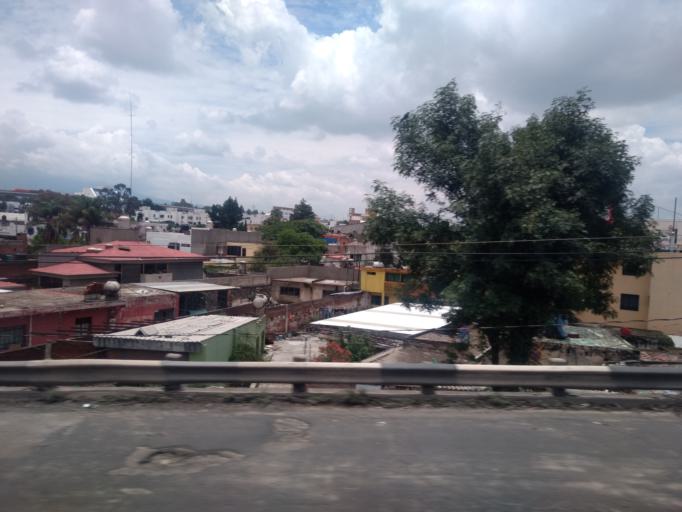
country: MX
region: Puebla
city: Puebla
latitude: 19.0826
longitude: -98.2049
